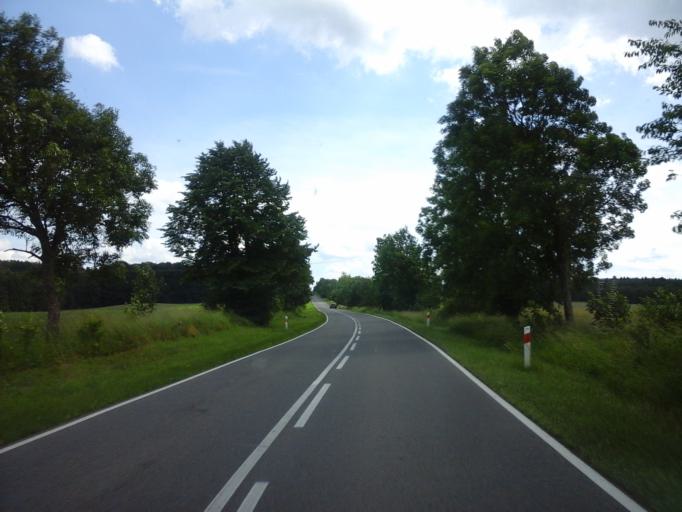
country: PL
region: West Pomeranian Voivodeship
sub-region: Powiat swidwinski
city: Slawoborze
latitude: 53.8493
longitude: 15.7349
